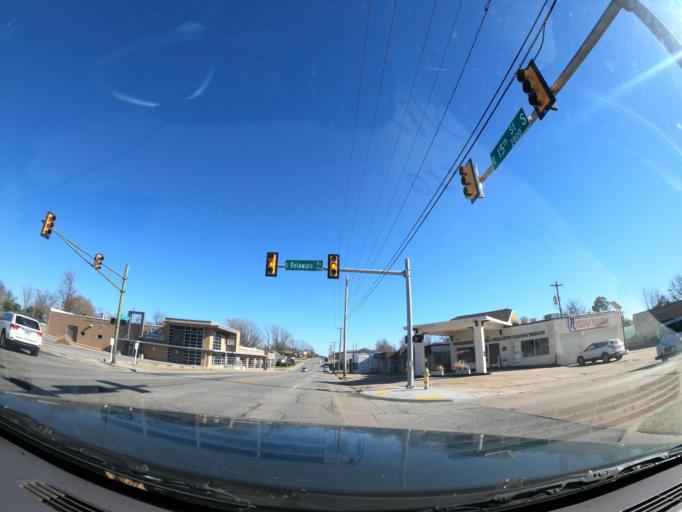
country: US
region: Oklahoma
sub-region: Tulsa County
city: Tulsa
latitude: 36.1405
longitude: -95.9494
